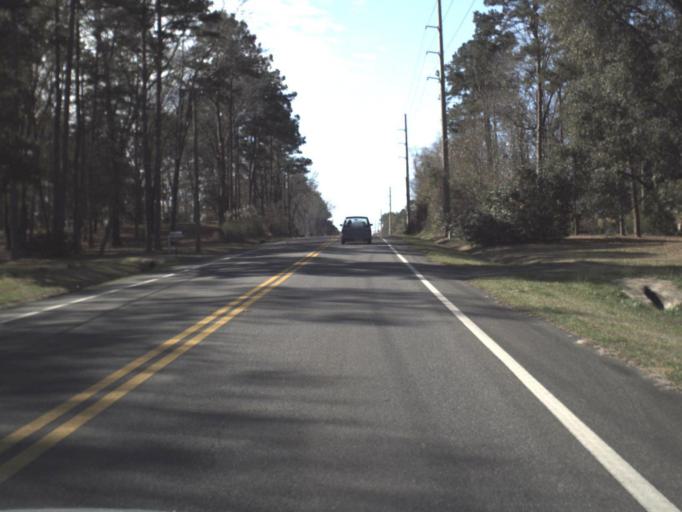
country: US
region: Florida
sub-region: Jackson County
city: Marianna
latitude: 30.8012
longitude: -85.1798
